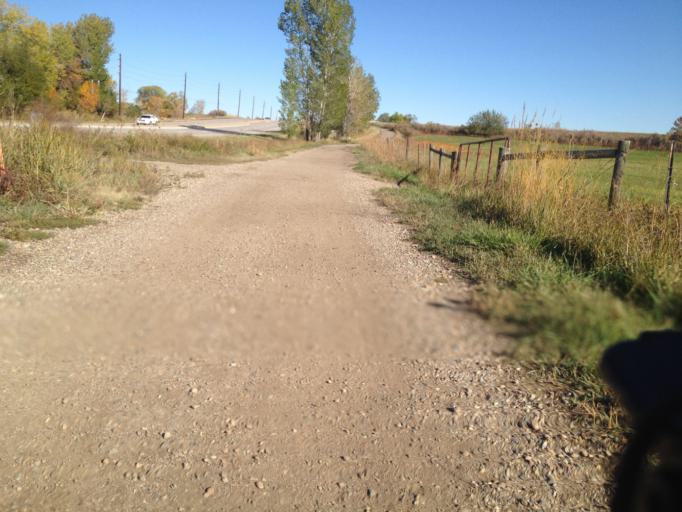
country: US
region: Colorado
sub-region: Boulder County
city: Boulder
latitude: 39.9857
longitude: -105.2192
